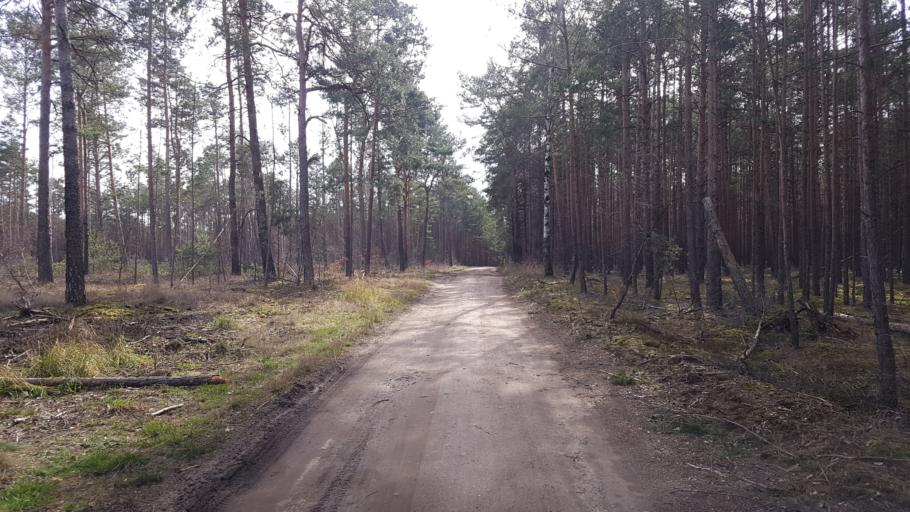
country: DE
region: Brandenburg
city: Doberlug-Kirchhain
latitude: 51.6261
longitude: 13.6060
